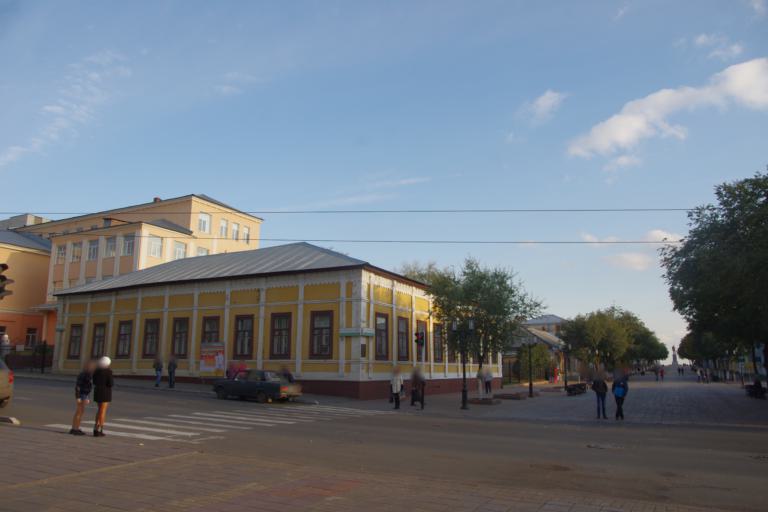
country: RU
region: Orenburg
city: Orenburg
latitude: 51.7579
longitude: 55.1042
